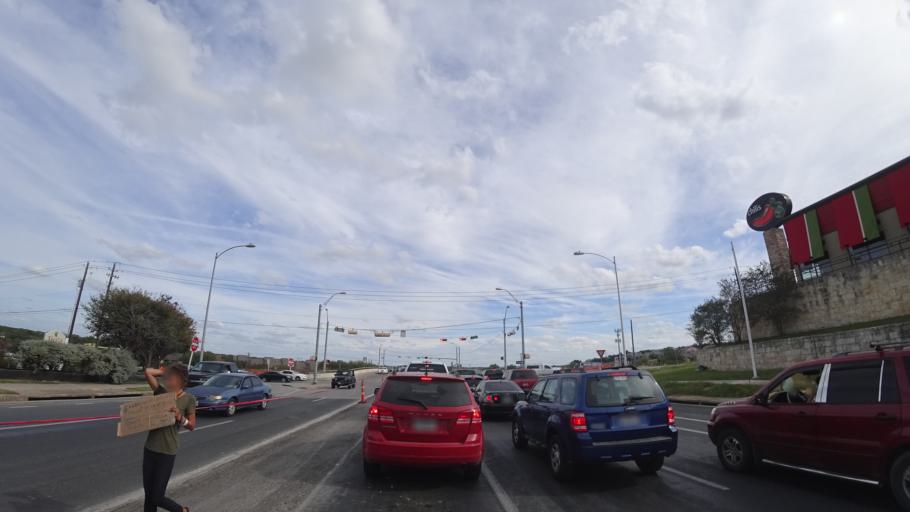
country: US
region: Texas
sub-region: Travis County
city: Onion Creek
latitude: 30.1989
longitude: -97.7648
